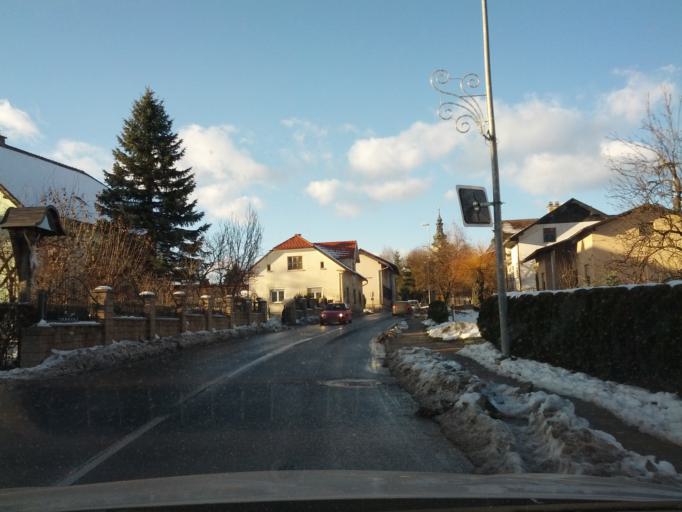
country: SI
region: Moravce
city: Moravce
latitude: 46.1338
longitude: 14.7453
